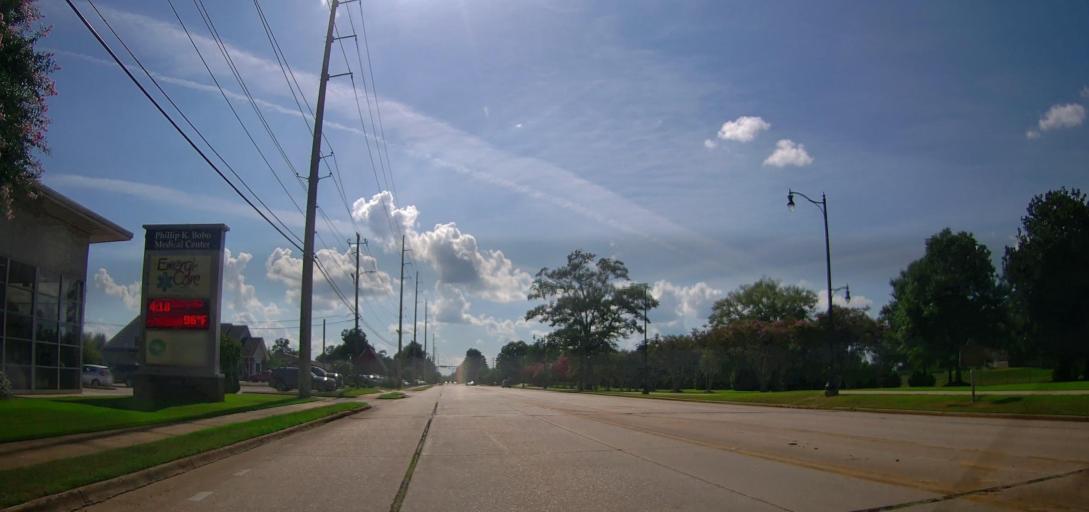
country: US
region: Alabama
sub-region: Tuscaloosa County
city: Holt
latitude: 33.2060
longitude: -87.5155
